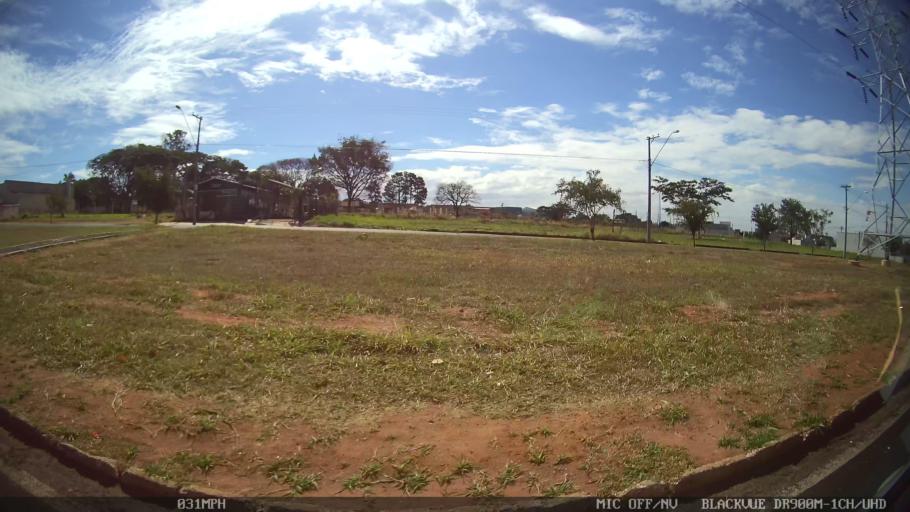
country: BR
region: Sao Paulo
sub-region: Sao Jose Do Rio Preto
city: Sao Jose do Rio Preto
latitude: -20.8162
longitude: -49.4897
